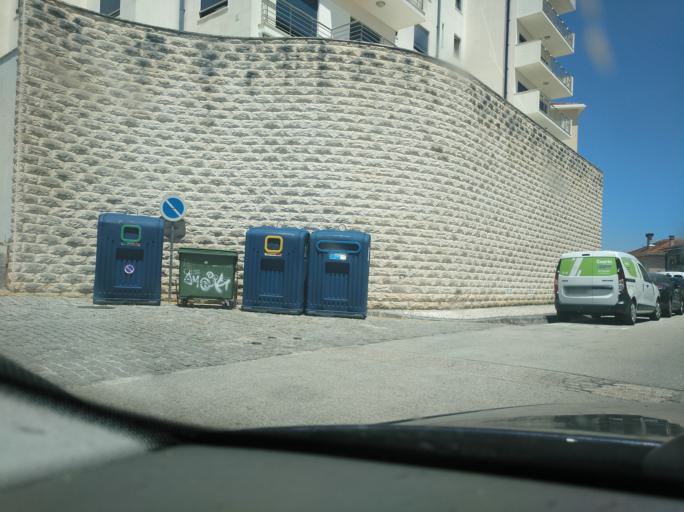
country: PT
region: Coimbra
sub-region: Coimbra
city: Coimbra
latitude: 40.2124
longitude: -8.4172
